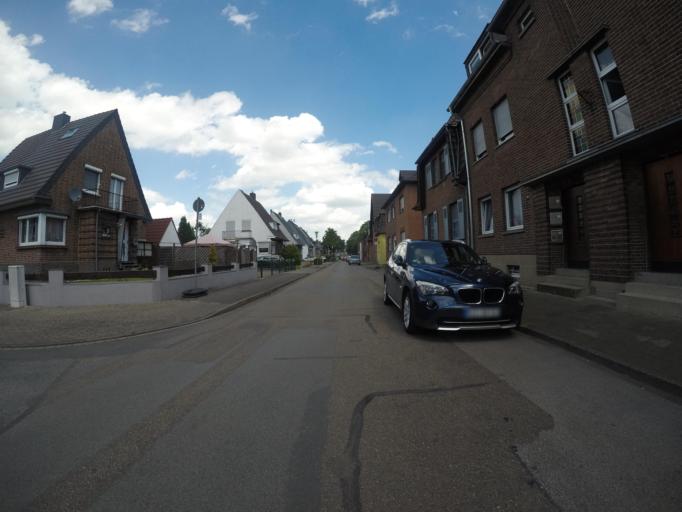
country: DE
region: North Rhine-Westphalia
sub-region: Regierungsbezirk Dusseldorf
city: Kleve
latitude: 51.7769
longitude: 6.1275
